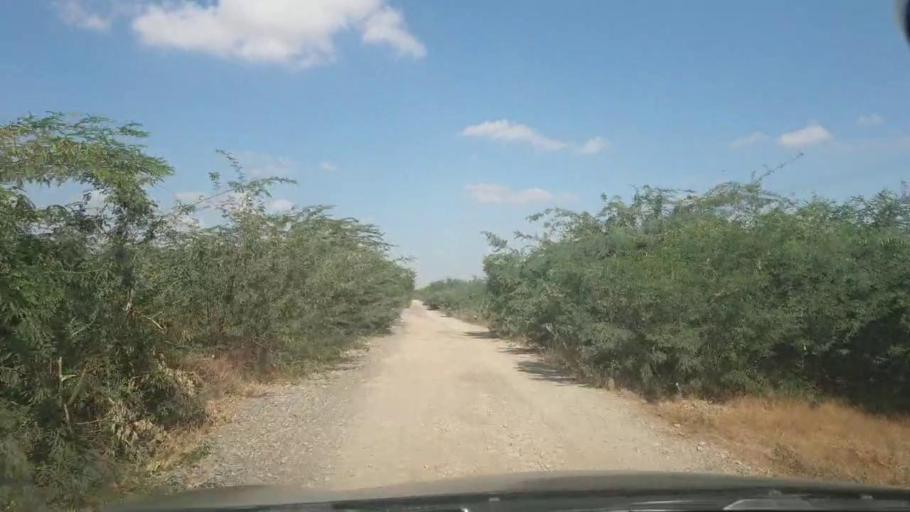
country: PK
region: Sindh
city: Malir Cantonment
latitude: 25.0626
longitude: 67.3957
